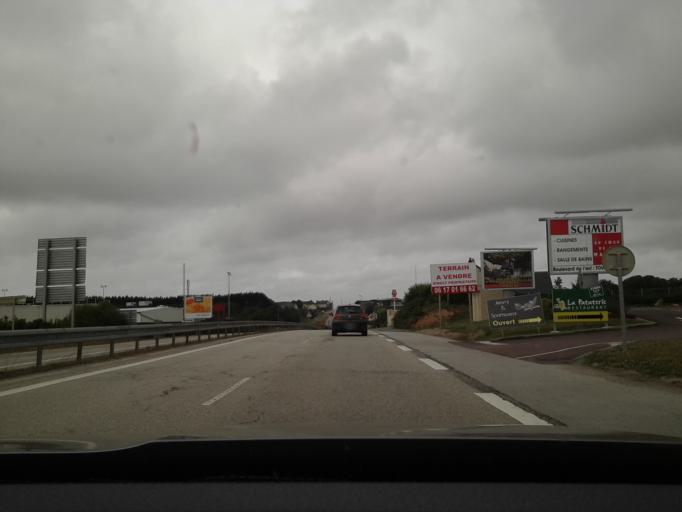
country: FR
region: Lower Normandy
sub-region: Departement de la Manche
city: La Glacerie
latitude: 49.6026
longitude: -1.5981
